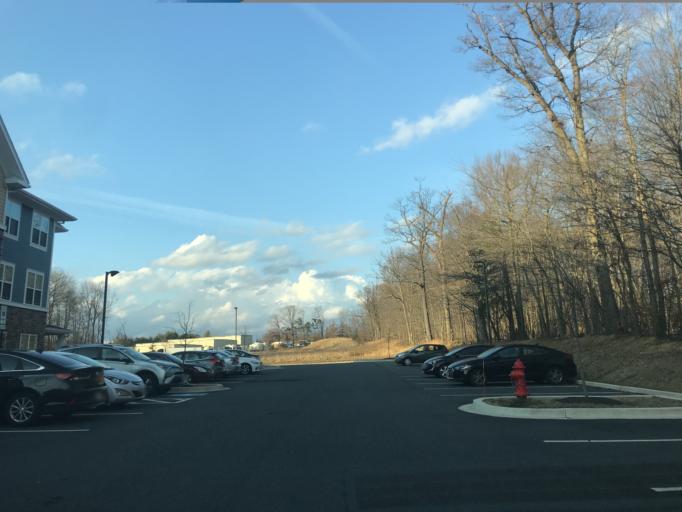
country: US
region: Maryland
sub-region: Harford County
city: Joppatowne
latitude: 39.4581
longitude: -76.3144
